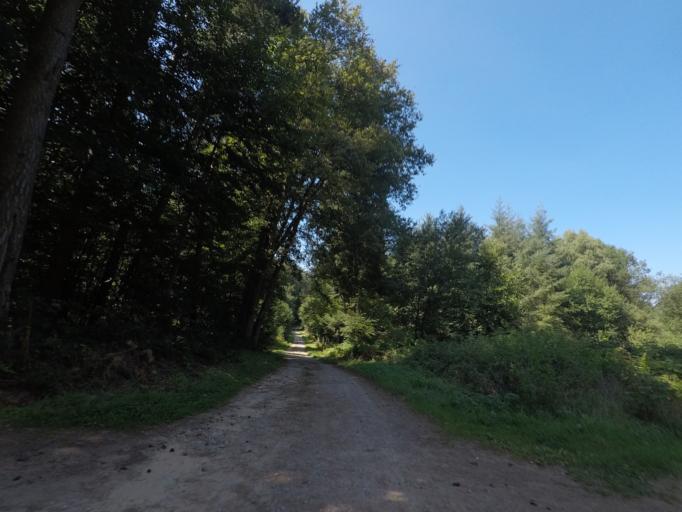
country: LU
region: Luxembourg
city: Bridel
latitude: 49.6464
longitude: 6.0836
